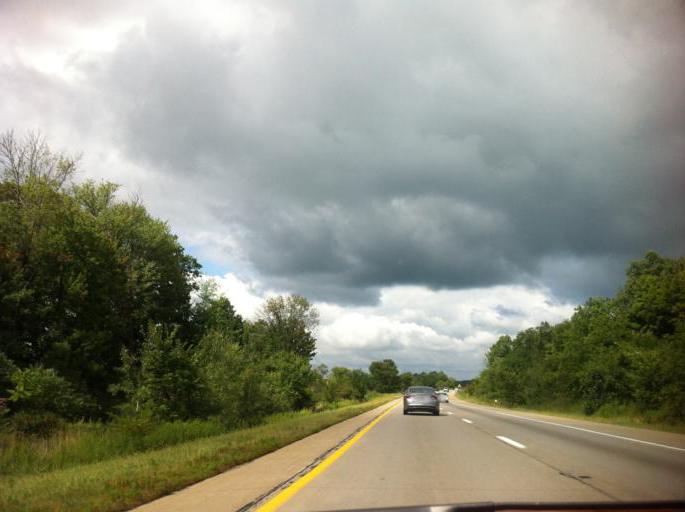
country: US
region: Pennsylvania
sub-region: Lawrence County
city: New Wilmington
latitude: 41.1857
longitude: -80.3577
